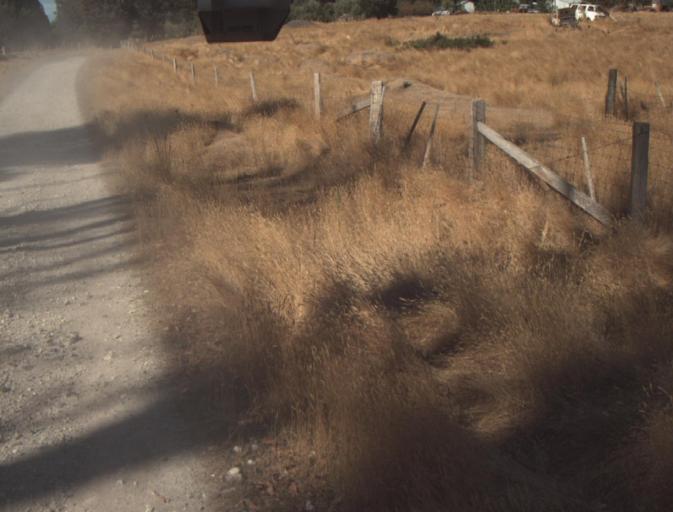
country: AU
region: Tasmania
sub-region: Launceston
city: Mayfield
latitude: -41.1567
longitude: 147.2045
